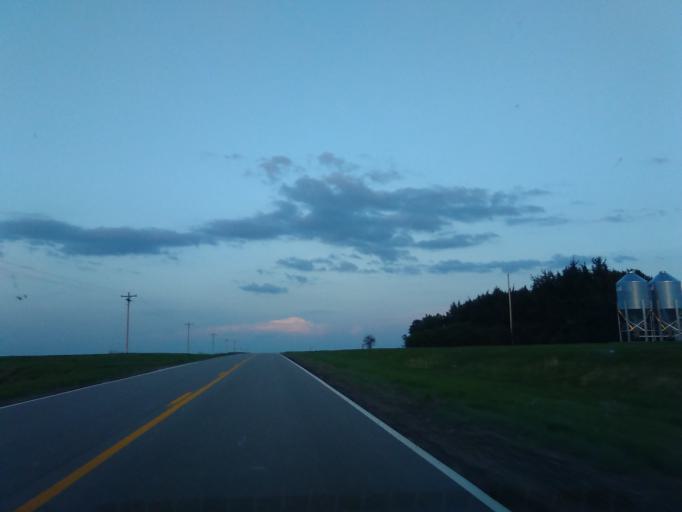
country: US
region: Nebraska
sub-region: Nuckolls County
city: Nelson
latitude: 40.2928
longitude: -98.1856
